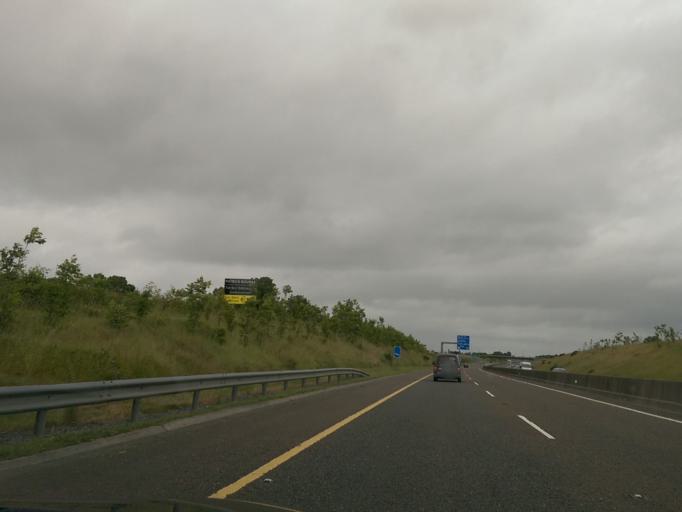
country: IE
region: Munster
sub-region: An Clar
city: Ennis
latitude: 52.8199
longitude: -8.9377
